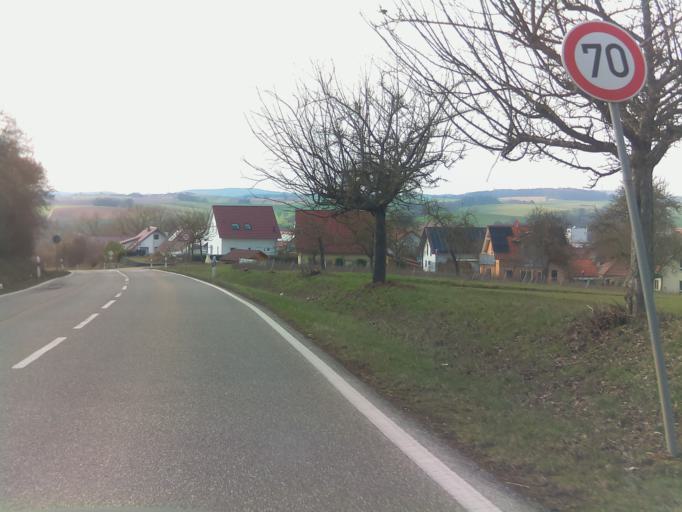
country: DE
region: Baden-Wuerttemberg
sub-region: Regierungsbezirk Stuttgart
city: Ittlingen
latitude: 49.1684
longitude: 8.9500
